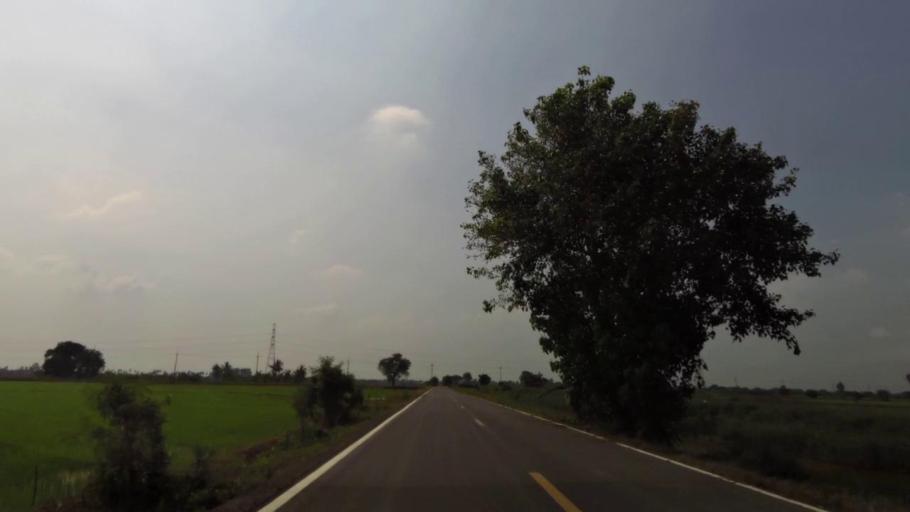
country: TH
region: Ang Thong
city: Pho Thong
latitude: 14.6206
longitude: 100.4030
